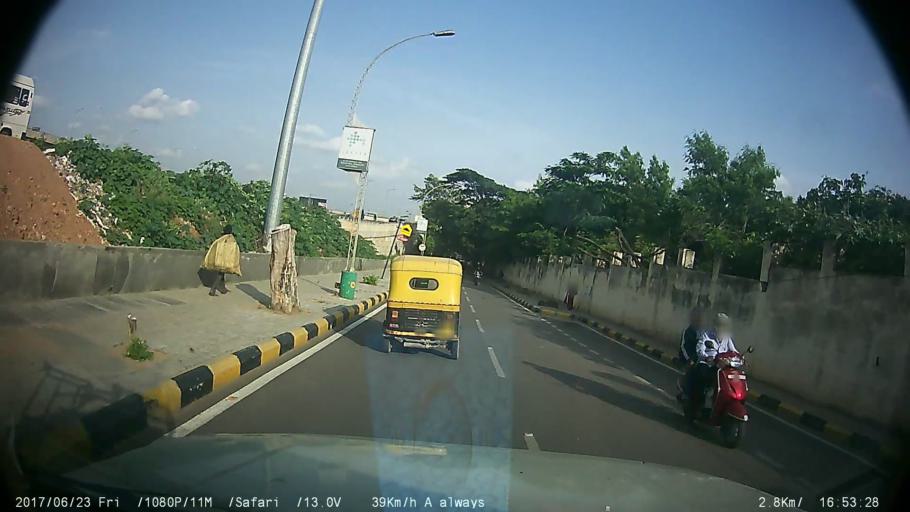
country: IN
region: Karnataka
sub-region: Bangalore Urban
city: Anekal
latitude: 12.8456
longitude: 77.6716
